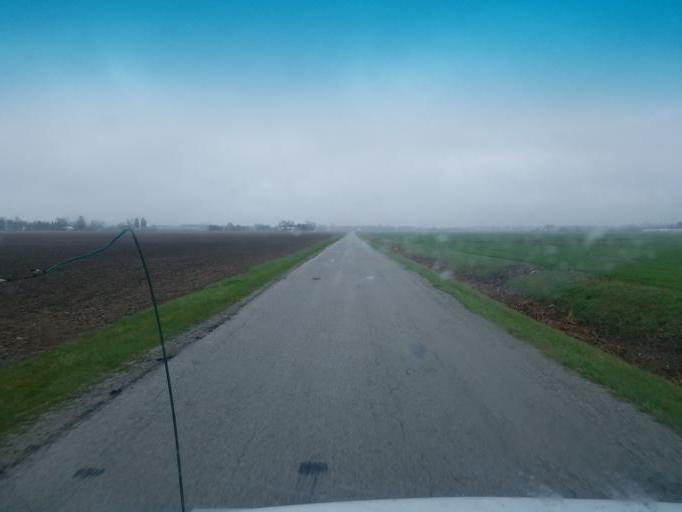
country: US
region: Ohio
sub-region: Wood County
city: North Baltimore
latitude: 41.2602
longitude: -83.6312
